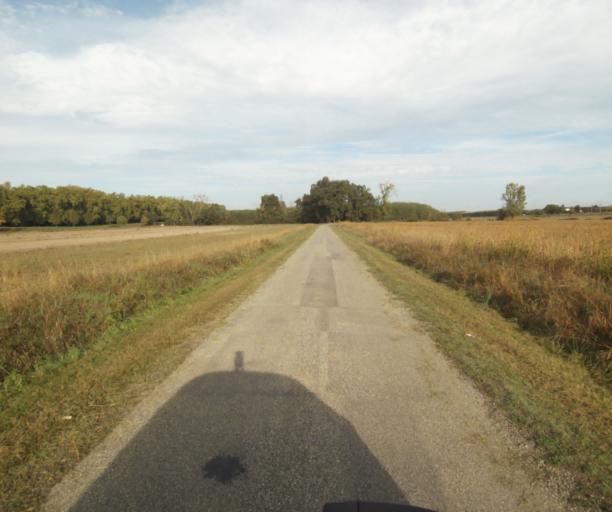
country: FR
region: Midi-Pyrenees
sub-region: Departement du Tarn-et-Garonne
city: Montech
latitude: 43.9754
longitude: 1.2242
